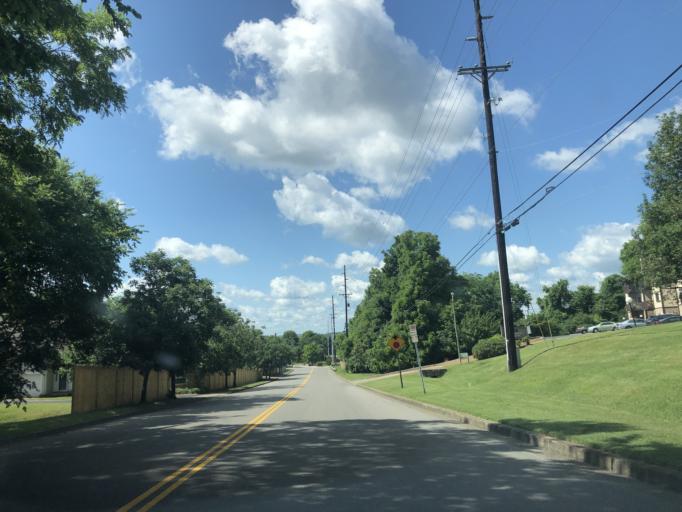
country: US
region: Tennessee
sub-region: Davidson County
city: Belle Meade
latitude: 36.0644
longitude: -86.9235
